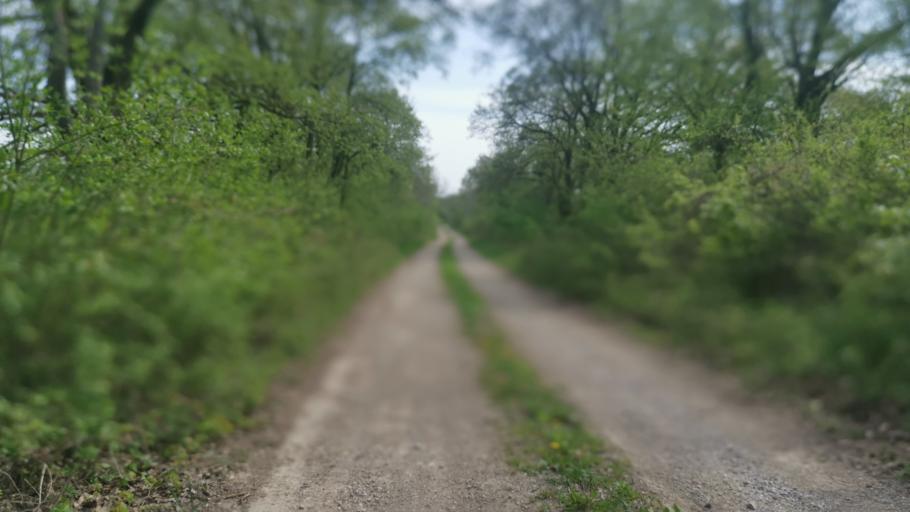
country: SK
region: Trnavsky
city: Smolenice
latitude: 48.5423
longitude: 17.4437
